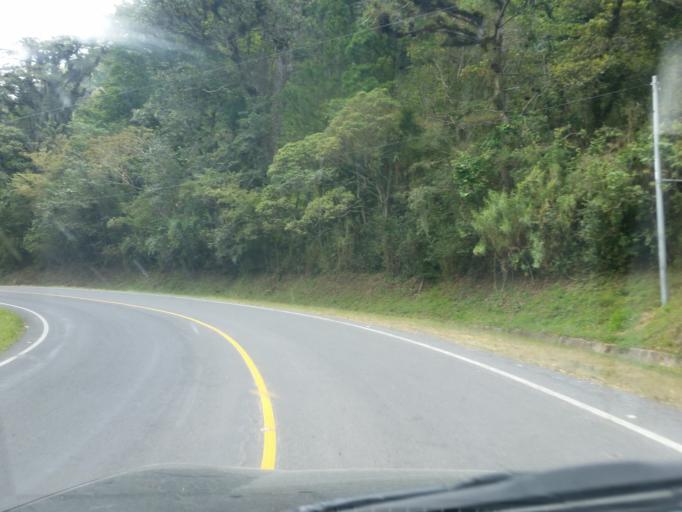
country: NI
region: Matagalpa
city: Matagalpa
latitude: 12.9944
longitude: -85.9222
